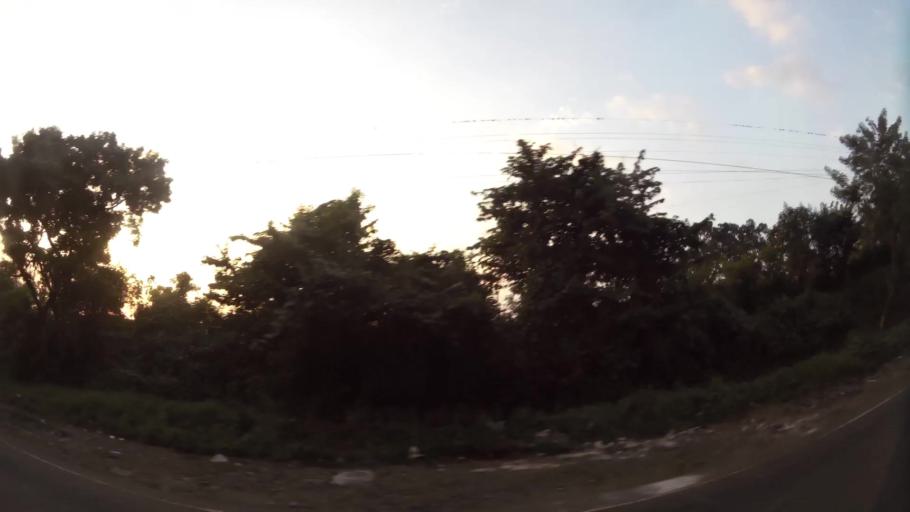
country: GT
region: Retalhuleu
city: Santa Cruz Mulua
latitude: 14.5804
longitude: -91.6281
